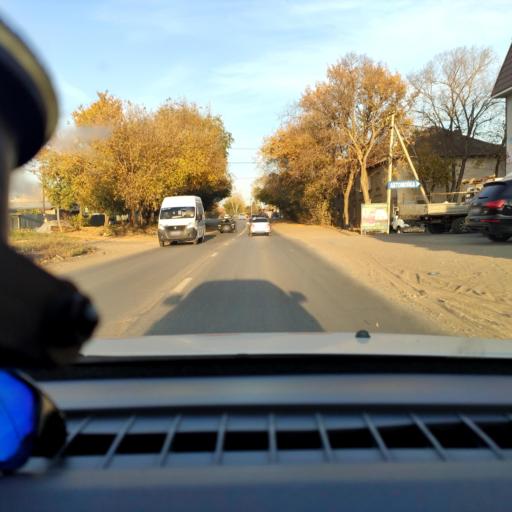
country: RU
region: Samara
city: Samara
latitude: 53.1749
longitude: 50.1773
